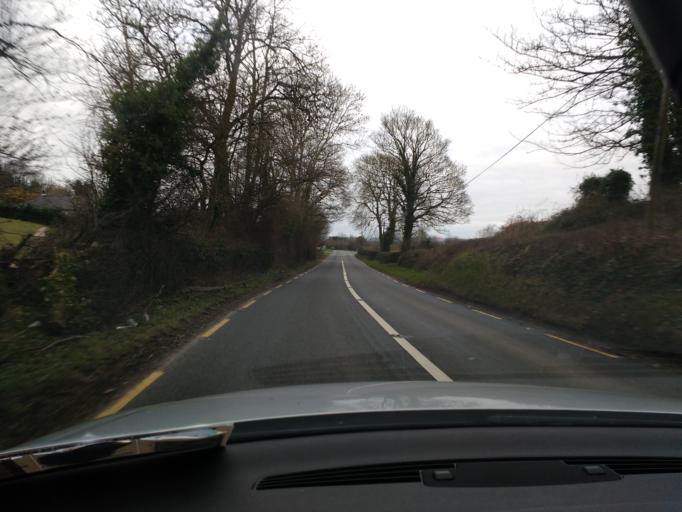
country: IE
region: Leinster
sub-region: Kilkenny
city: Kilkenny
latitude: 52.6850
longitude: -7.2752
